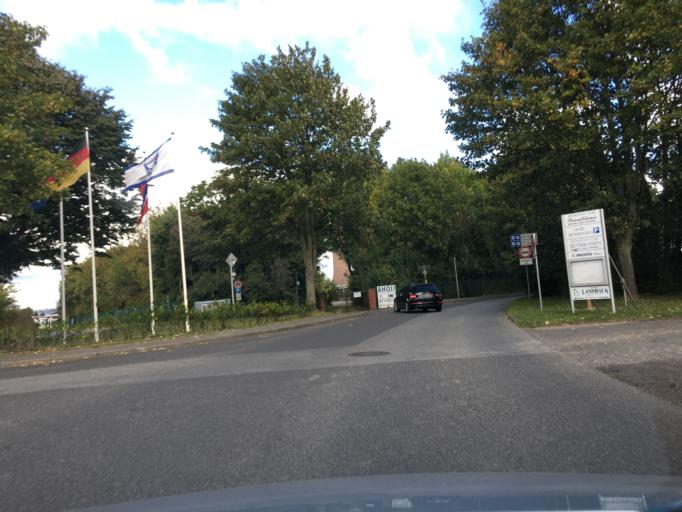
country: DE
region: Schleswig-Holstein
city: Laboe
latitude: 54.4100
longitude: 10.2333
